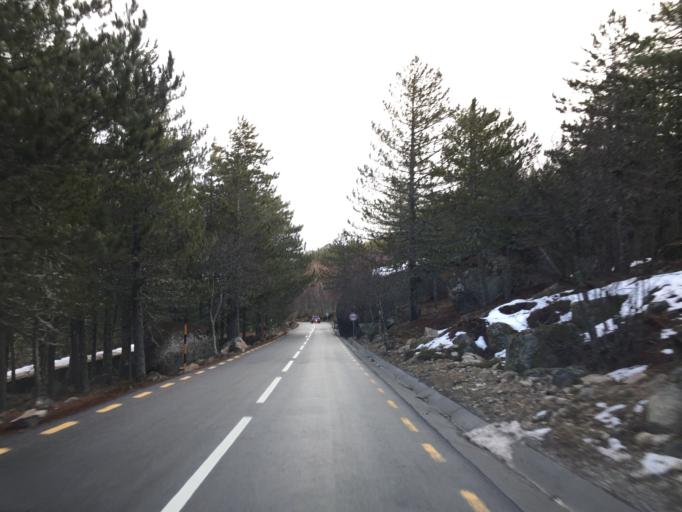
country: PT
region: Castelo Branco
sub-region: Covilha
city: Covilha
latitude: 40.3225
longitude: -7.5736
